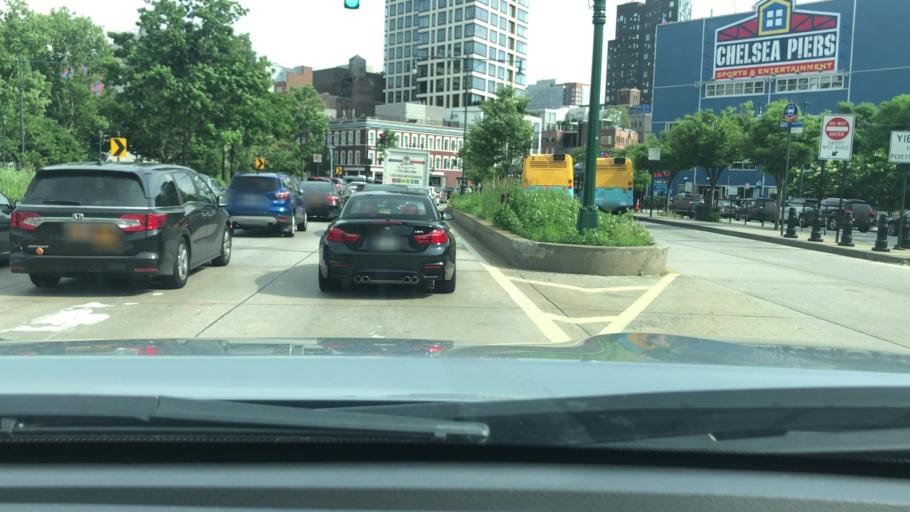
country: US
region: New Jersey
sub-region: Hudson County
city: Weehawken
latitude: 40.7494
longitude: -74.0083
